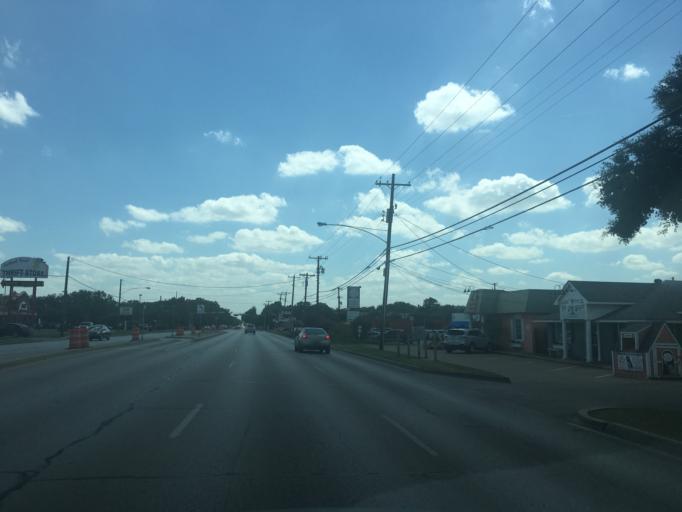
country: US
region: Texas
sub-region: Dallas County
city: Garland
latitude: 32.8398
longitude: -96.6949
